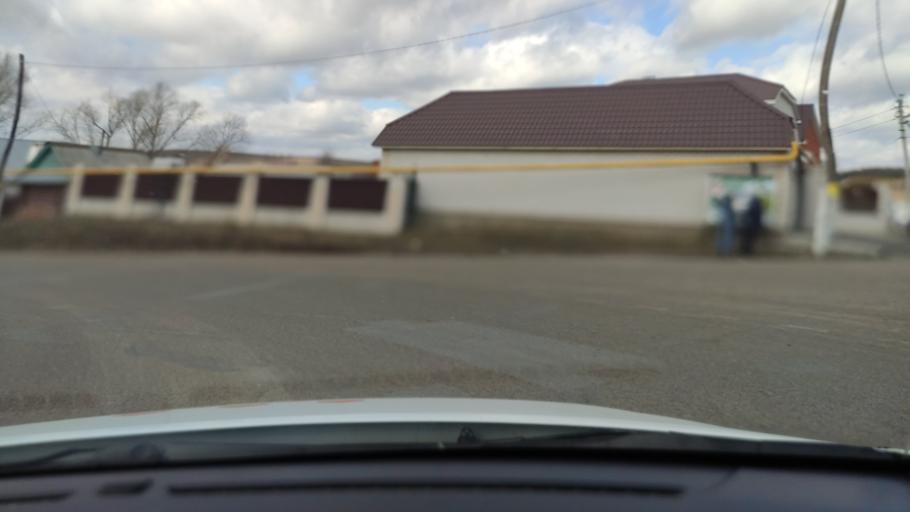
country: RU
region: Tatarstan
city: Vysokaya Gora
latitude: 56.1235
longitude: 49.1965
